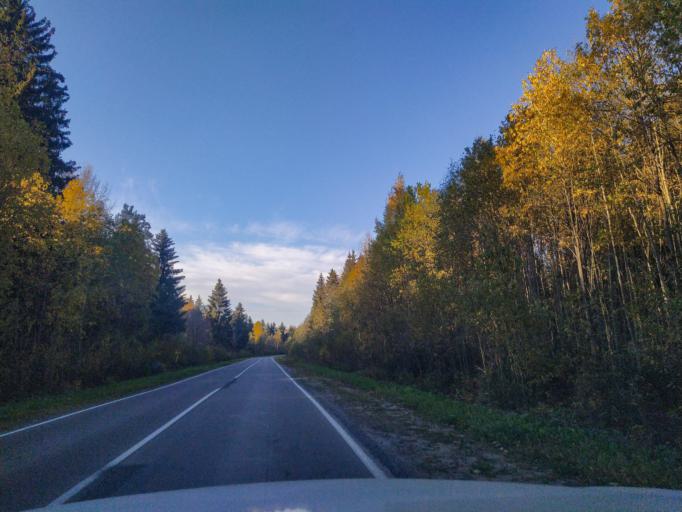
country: RU
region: Leningrad
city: Siverskiy
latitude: 59.3062
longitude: 30.0316
